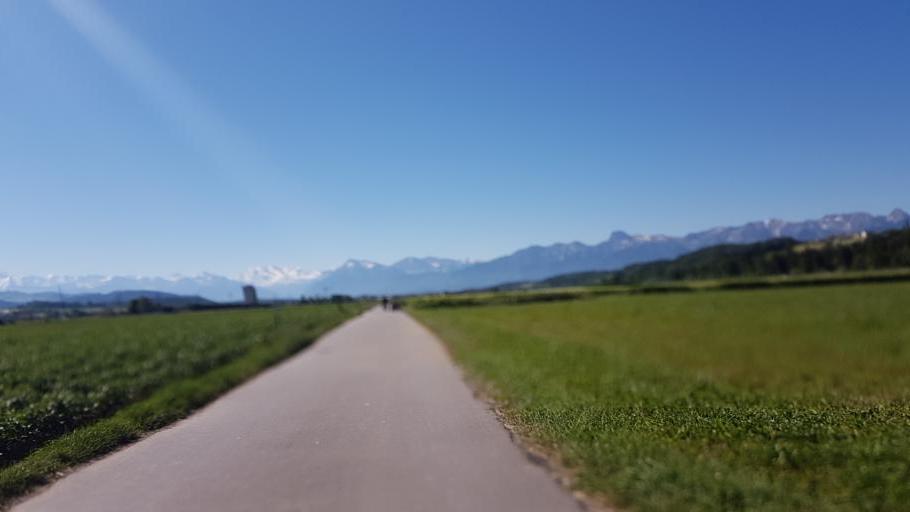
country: CH
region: Bern
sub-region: Bern-Mittelland District
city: Niederwichtrach
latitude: 46.8554
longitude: 7.5609
